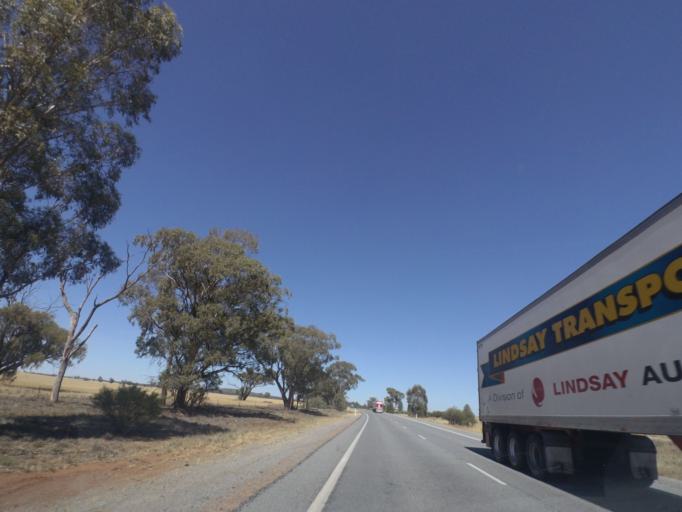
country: AU
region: New South Wales
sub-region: Narrandera
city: Narrandera
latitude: -34.4124
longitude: 146.8723
